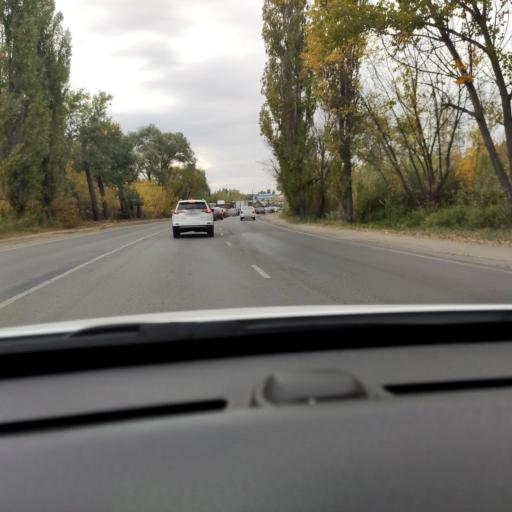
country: RU
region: Voronezj
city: Maslovka
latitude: 51.6219
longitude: 39.2549
